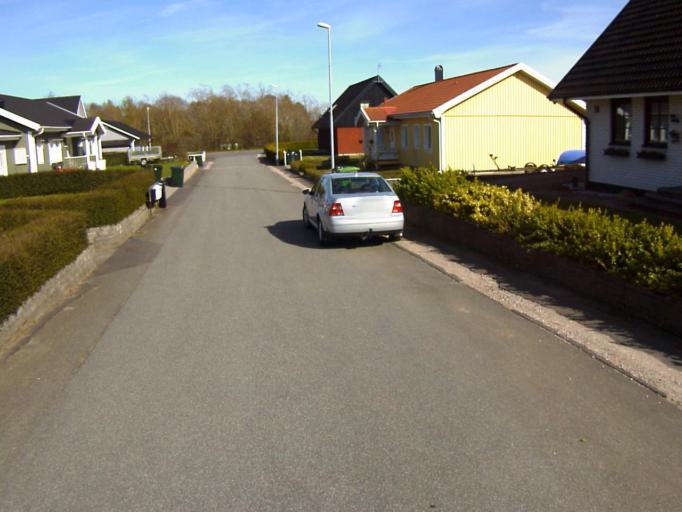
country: SE
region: Skane
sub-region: Kristianstads Kommun
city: Onnestad
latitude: 55.9971
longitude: 14.0356
